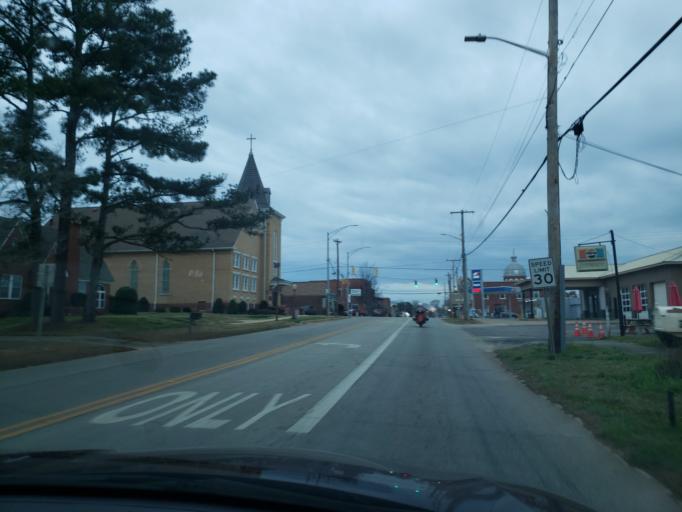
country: US
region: Alabama
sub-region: Chambers County
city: Lafayette
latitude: 32.8971
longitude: -85.4012
